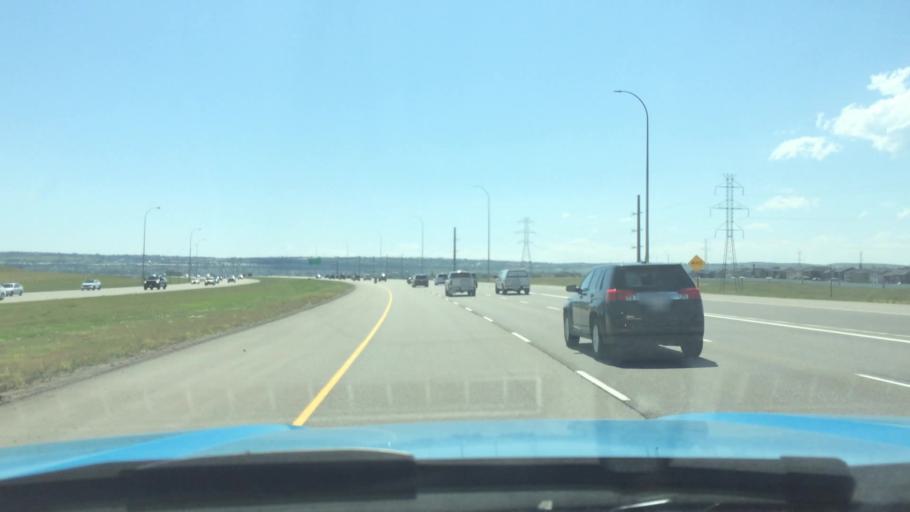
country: CA
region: Alberta
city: Calgary
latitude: 51.1714
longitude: -114.1004
